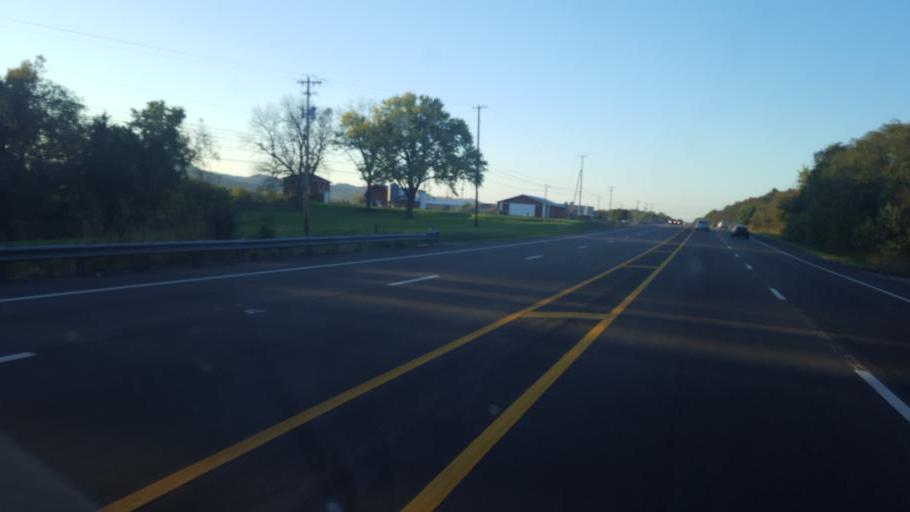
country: US
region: Ohio
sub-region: Scioto County
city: Lucasville
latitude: 38.8562
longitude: -82.9876
